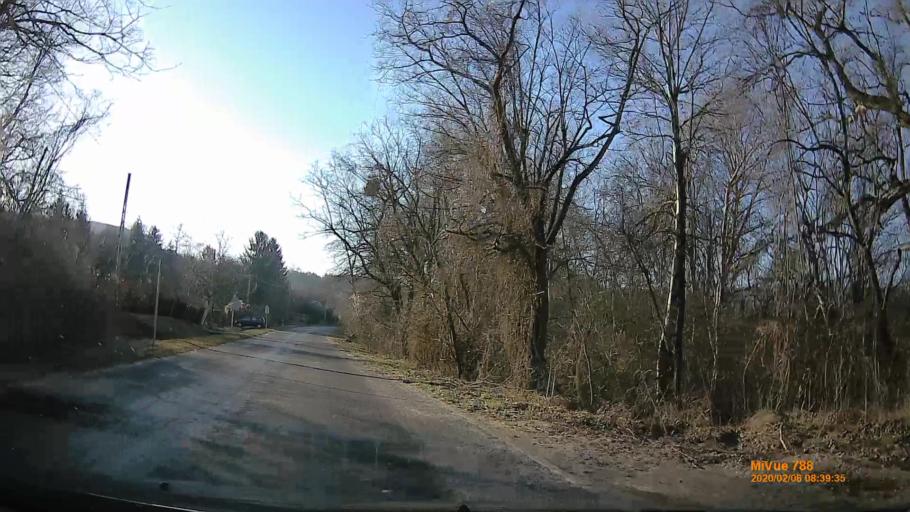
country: HU
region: Fejer
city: Szarliget
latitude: 47.5277
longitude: 18.4956
